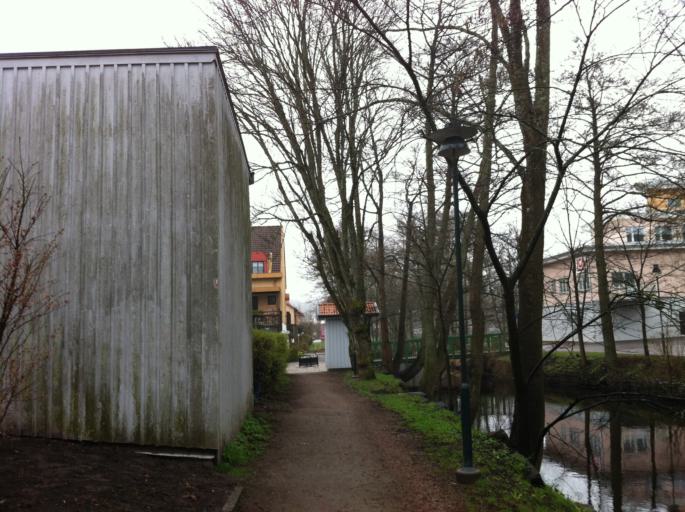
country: SE
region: Vaestra Goetaland
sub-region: Alingsas Kommun
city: Alingsas
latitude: 57.9280
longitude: 12.5352
